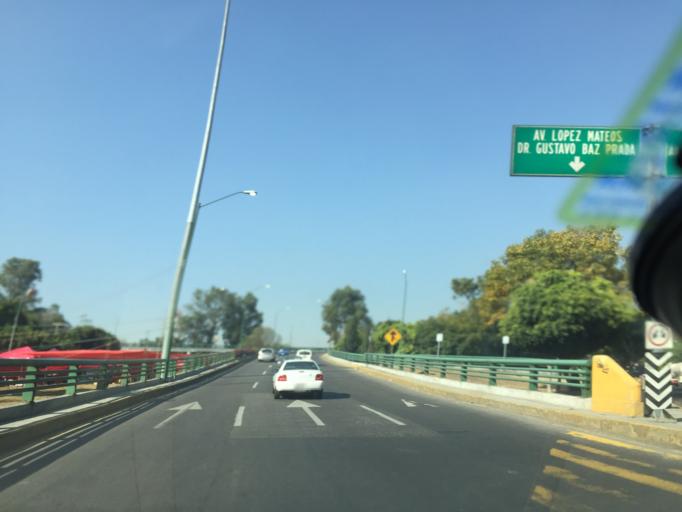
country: MX
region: Mexico
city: Vista Hermosa
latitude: 19.5087
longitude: -99.2088
